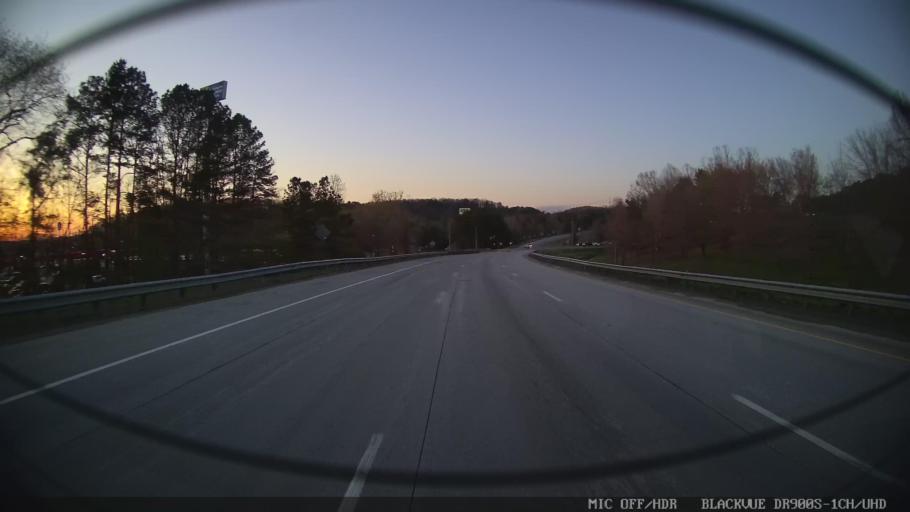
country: US
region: Georgia
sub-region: Bartow County
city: Cartersville
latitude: 34.2056
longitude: -84.7545
